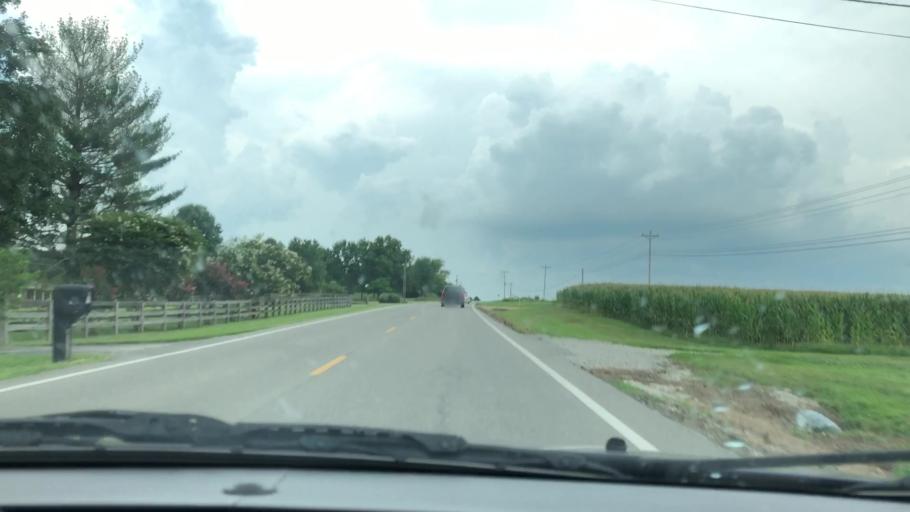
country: US
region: Tennessee
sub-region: Maury County
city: Columbia
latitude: 35.7065
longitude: -87.0157
